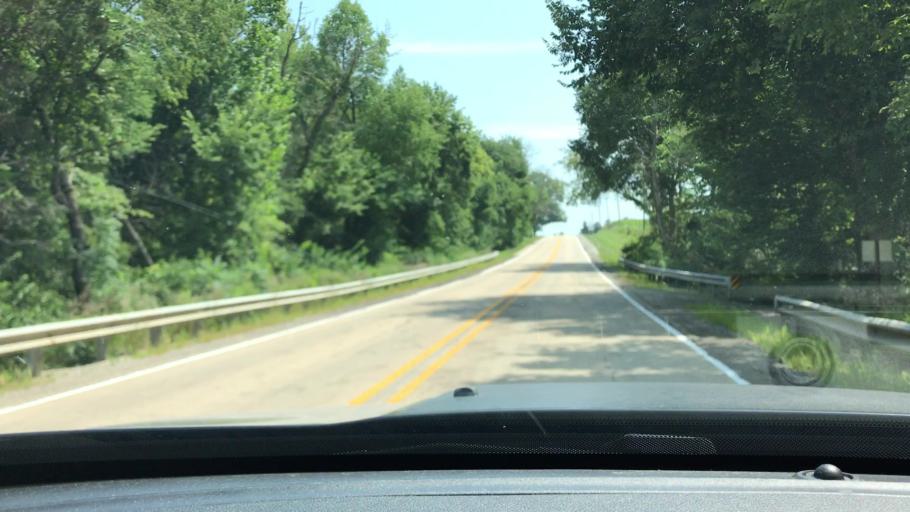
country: US
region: Illinois
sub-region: LaSalle County
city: Sheridan
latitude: 41.4852
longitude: -88.7727
